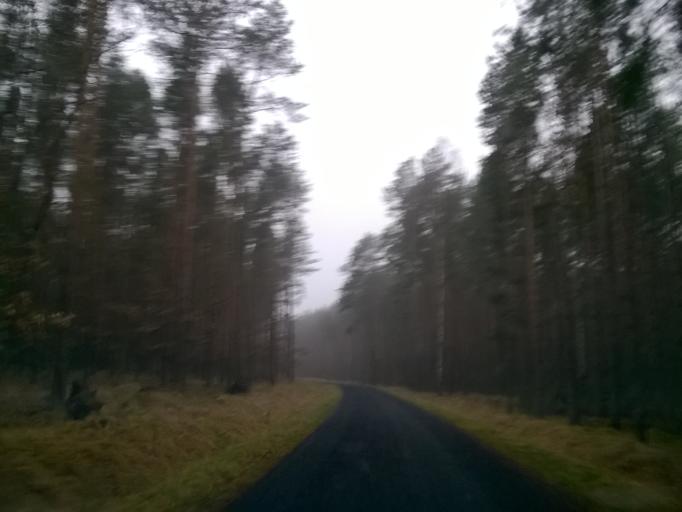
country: PL
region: Kujawsko-Pomorskie
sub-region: Powiat nakielski
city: Kcynia
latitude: 53.0495
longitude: 17.5529
